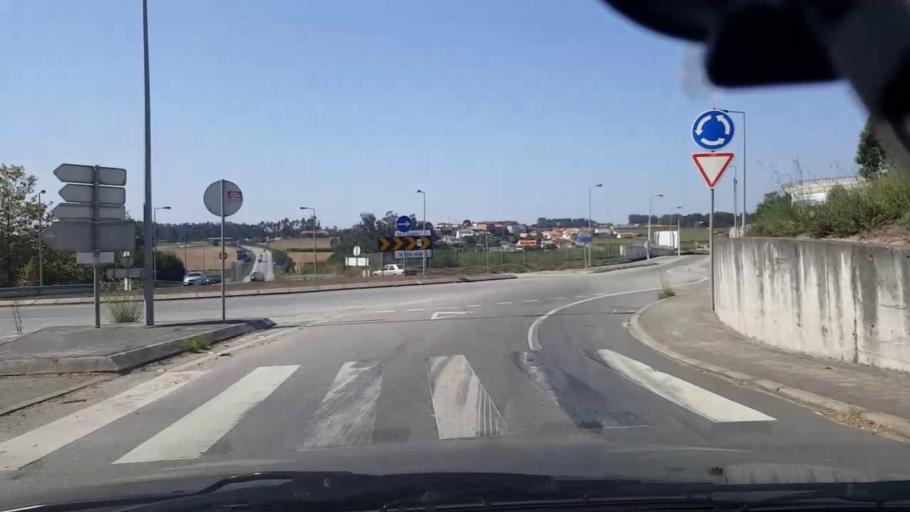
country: PT
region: Porto
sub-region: Vila do Conde
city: Vila do Conde
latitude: 41.3862
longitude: -8.7100
